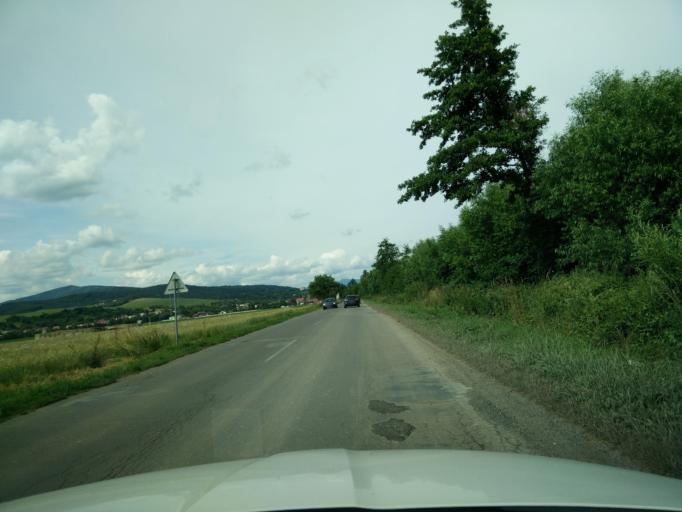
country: SK
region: Nitriansky
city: Bojnice
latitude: 48.7501
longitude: 18.5707
